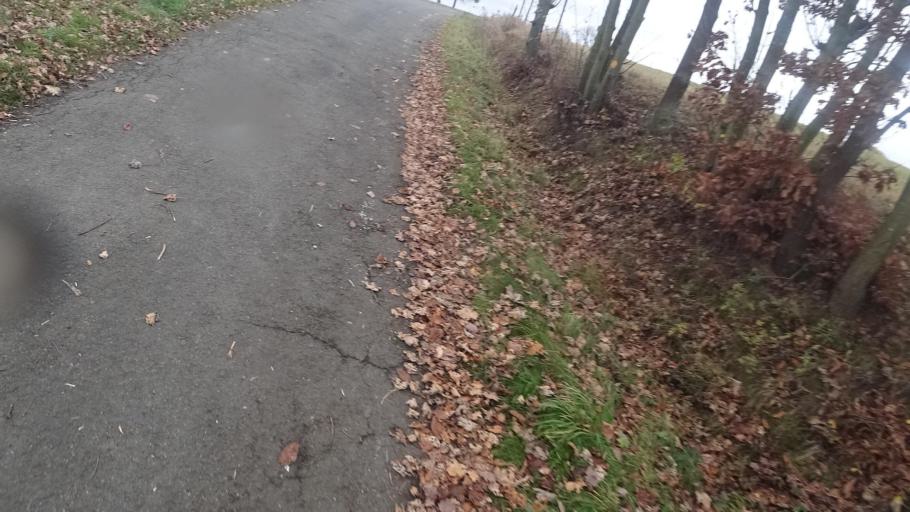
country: DE
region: Rheinland-Pfalz
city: Prath
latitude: 50.1627
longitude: 7.6798
